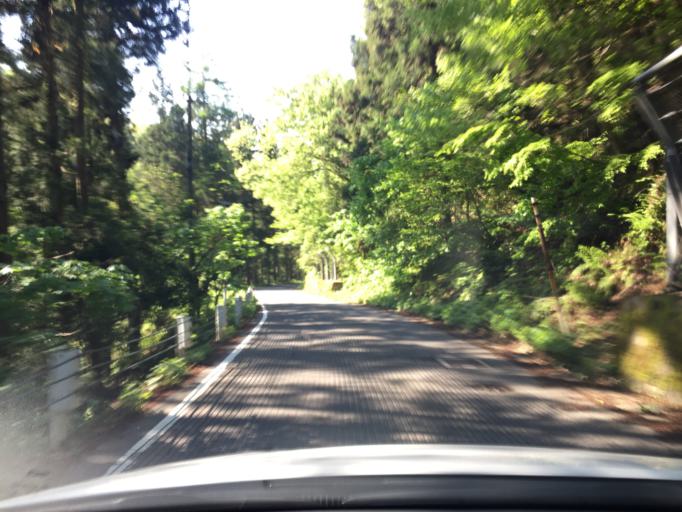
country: JP
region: Fukushima
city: Kitakata
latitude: 37.6676
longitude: 139.6151
